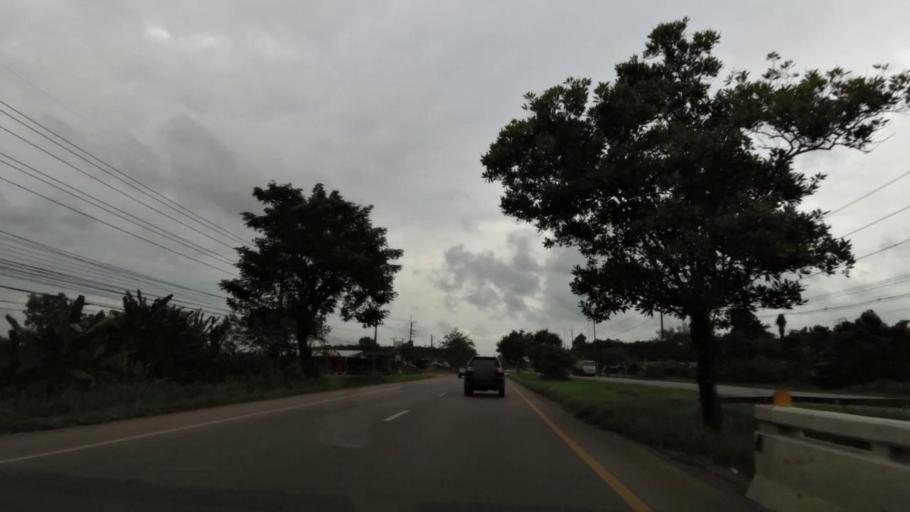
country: TH
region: Chanthaburi
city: Tha Mai
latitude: 12.7230
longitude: 101.9472
